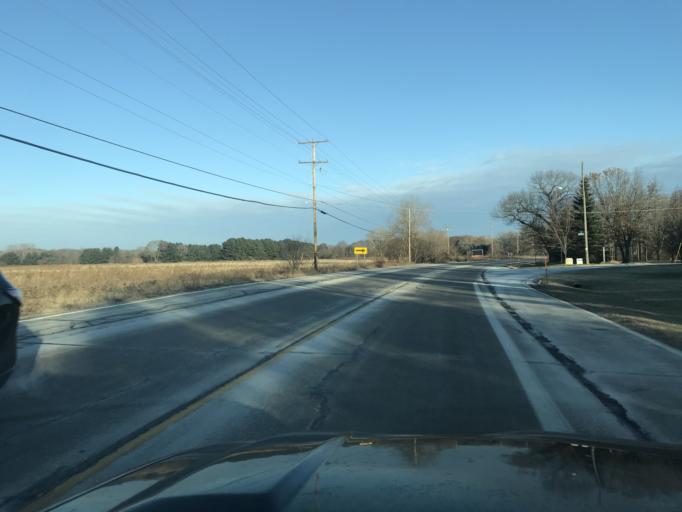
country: US
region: Illinois
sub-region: Lake County
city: Winthrop Harbor
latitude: 42.5300
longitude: -87.8259
